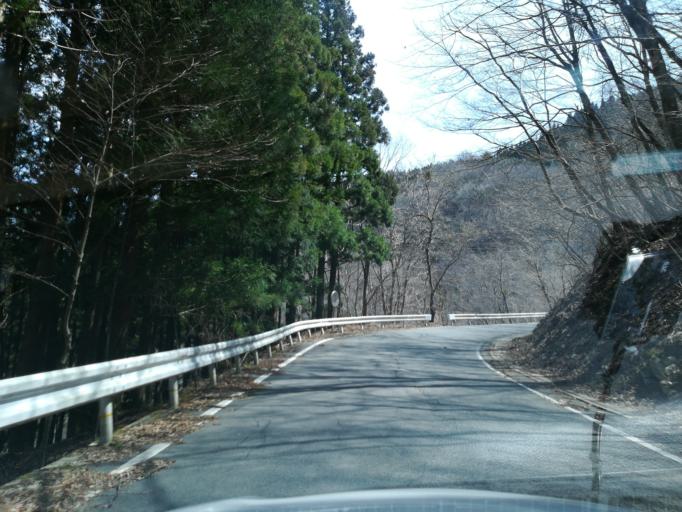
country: JP
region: Tokushima
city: Wakimachi
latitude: 33.8829
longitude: 134.0523
